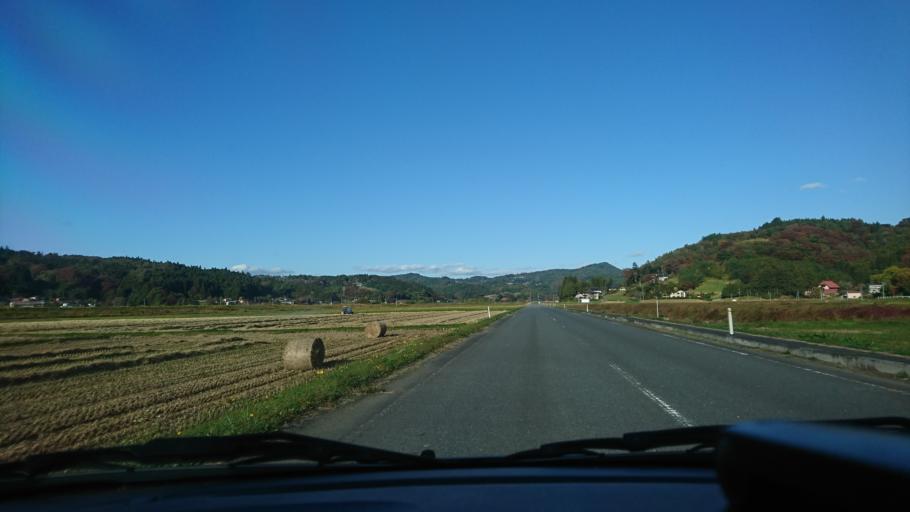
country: JP
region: Iwate
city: Ichinoseki
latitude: 38.8422
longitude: 141.2735
